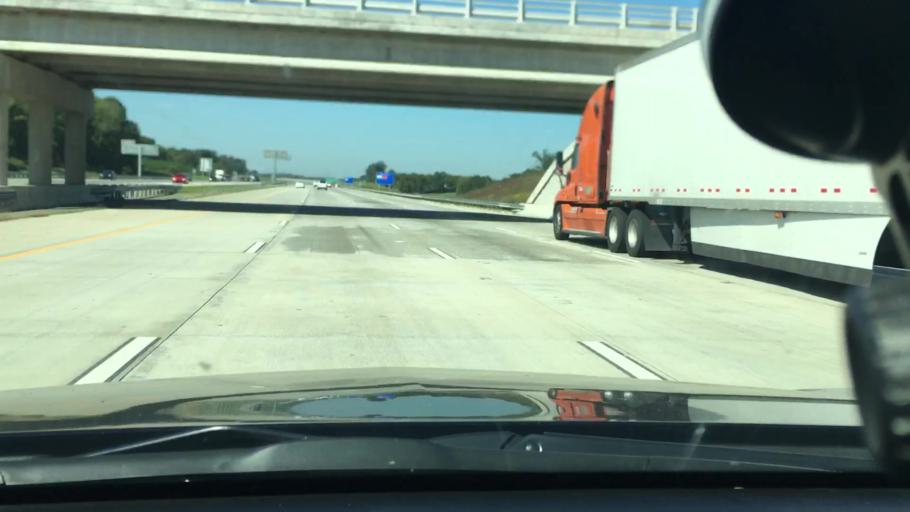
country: US
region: North Carolina
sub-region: Mecklenburg County
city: Huntersville
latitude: 35.3685
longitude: -80.7679
